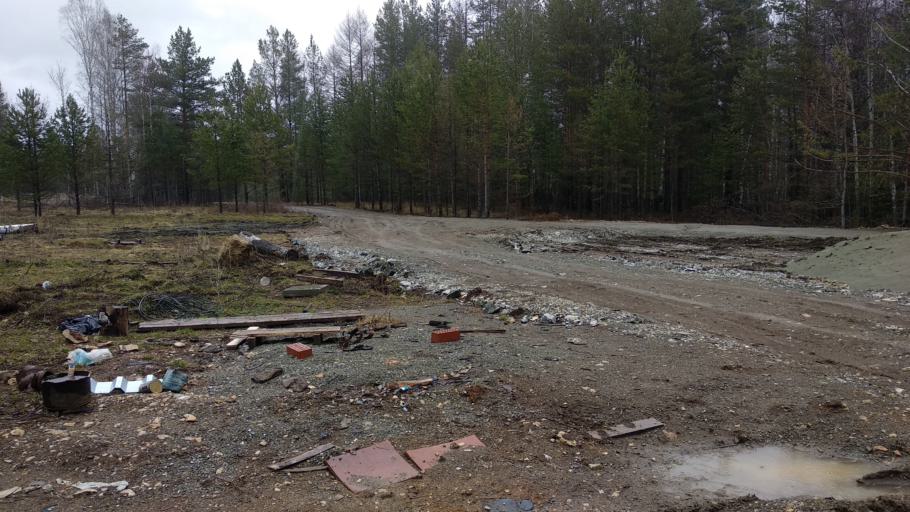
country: RU
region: Sverdlovsk
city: Krasnotur'insk
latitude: 59.6519
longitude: 60.1571
